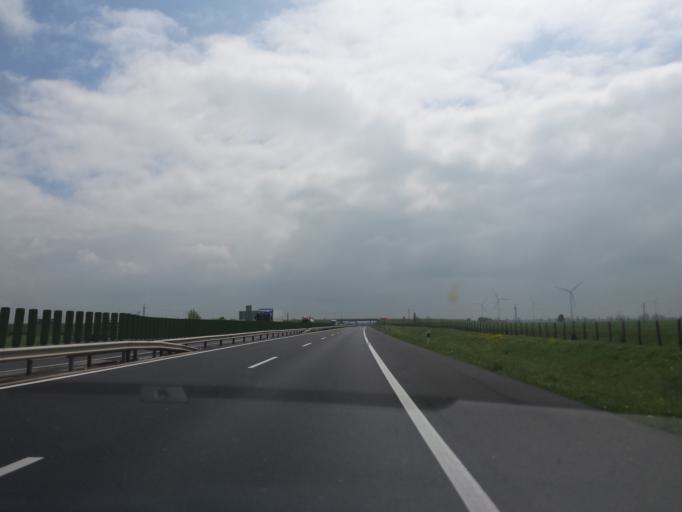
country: HU
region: Gyor-Moson-Sopron
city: Mosonmagyarovar
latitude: 47.8962
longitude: 17.1752
